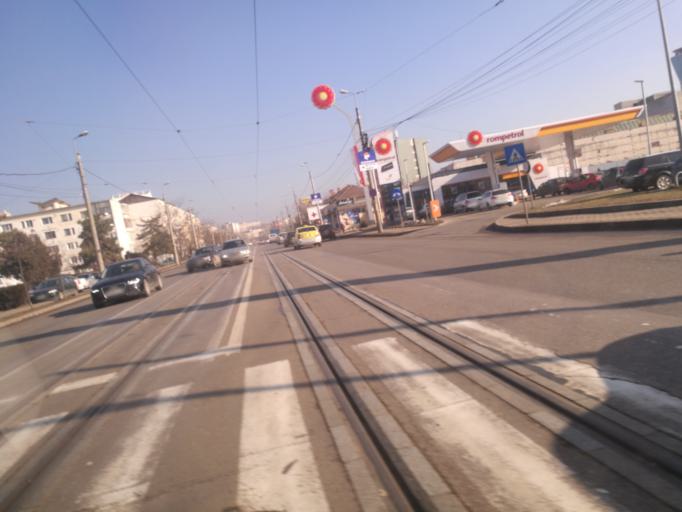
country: RO
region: Iasi
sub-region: Municipiul Iasi
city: Iasi
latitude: 47.1474
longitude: 27.5924
